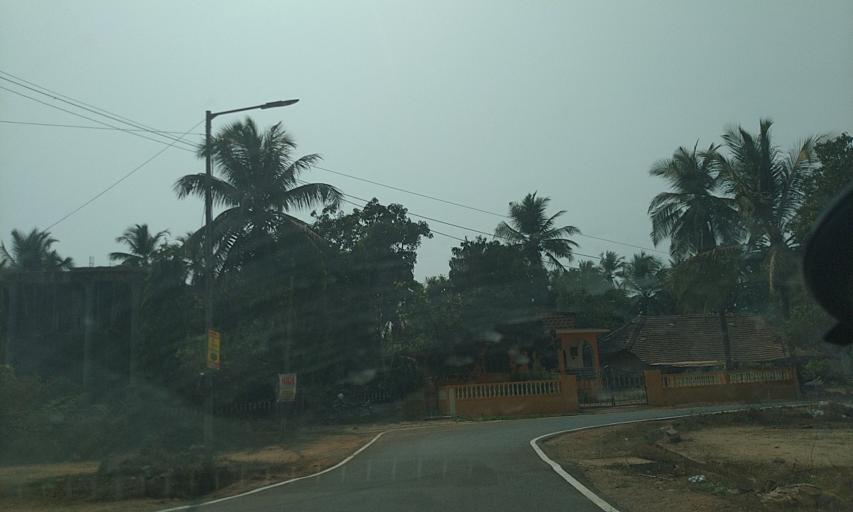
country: IN
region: Goa
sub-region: South Goa
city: Raia
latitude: 15.3013
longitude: 73.9466
